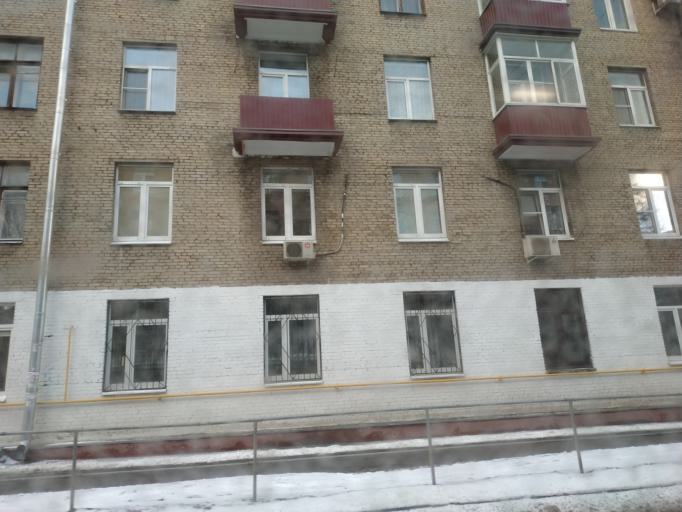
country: RU
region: Moskovskaya
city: Izmaylovo
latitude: 55.7940
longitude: 37.8192
